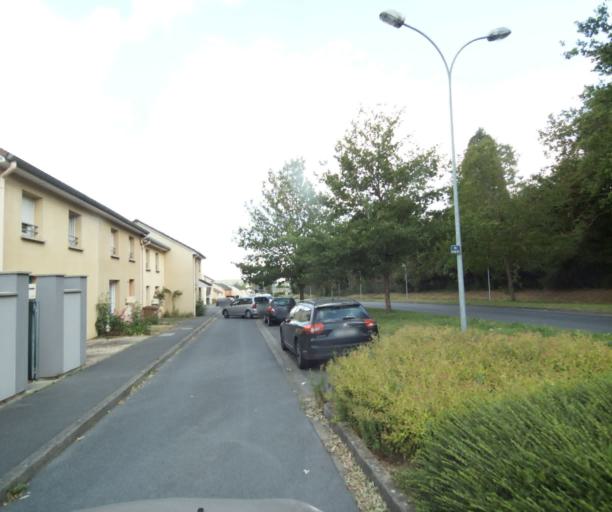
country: FR
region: Champagne-Ardenne
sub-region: Departement des Ardennes
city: Charleville-Mezieres
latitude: 49.7928
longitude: 4.7222
